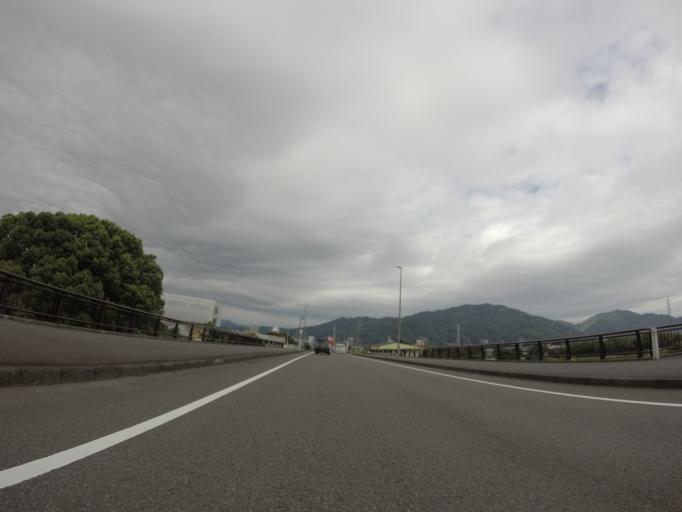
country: JP
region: Shizuoka
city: Yaizu
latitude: 34.8754
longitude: 138.3060
